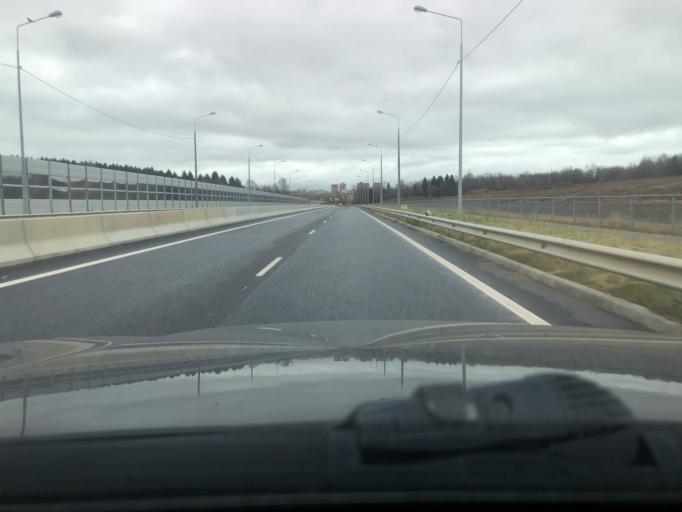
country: RU
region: Moskovskaya
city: Sergiyev Posad
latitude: 56.3374
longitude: 38.1033
